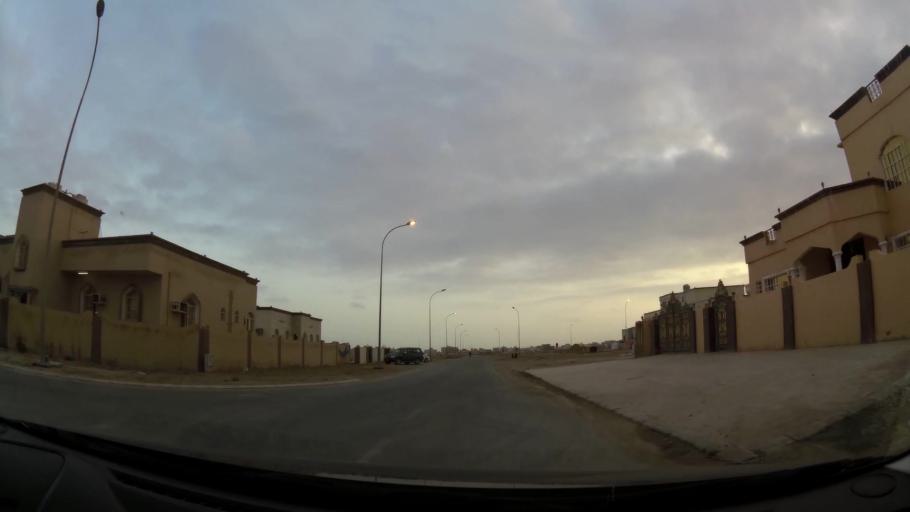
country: OM
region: Zufar
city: Salalah
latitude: 17.0309
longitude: 54.0208
